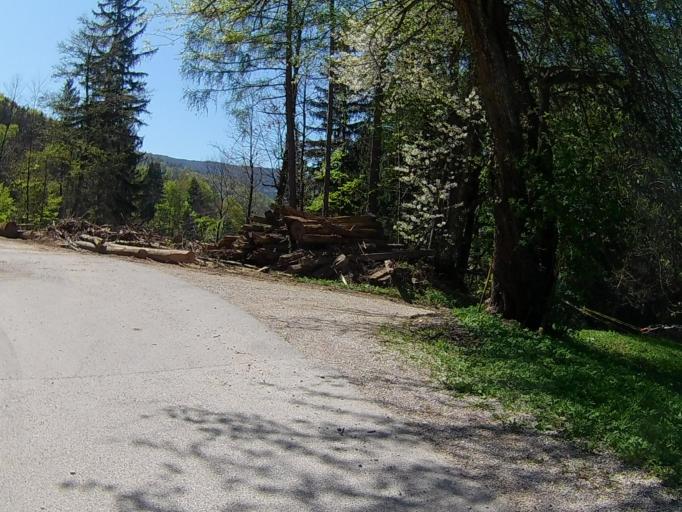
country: SI
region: Ruse
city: Ruse
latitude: 46.5264
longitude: 15.5084
